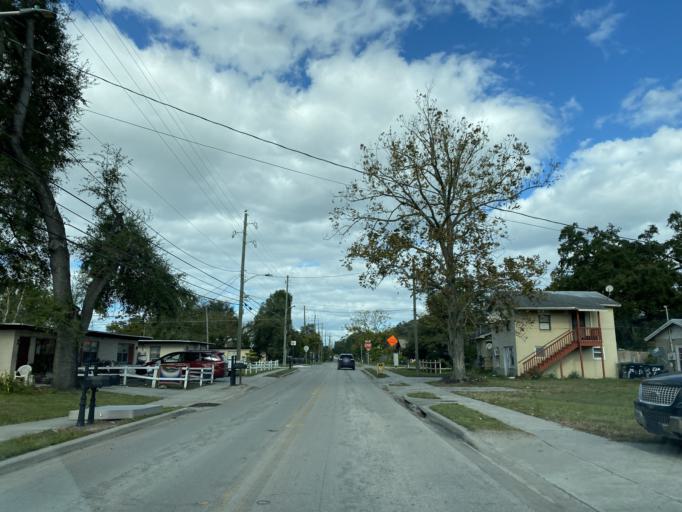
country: US
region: Florida
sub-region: Orange County
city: Orlando
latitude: 28.5222
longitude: -81.3929
